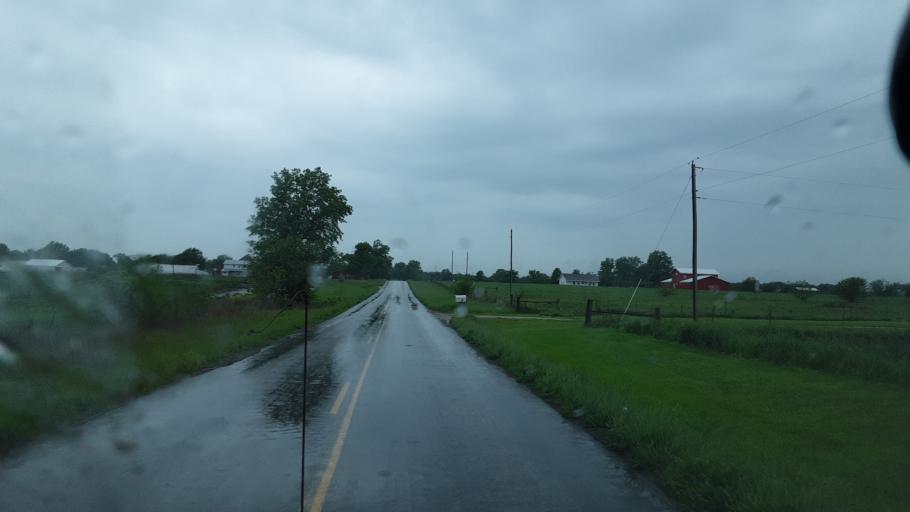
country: US
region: Missouri
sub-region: Randolph County
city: Moberly
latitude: 39.3682
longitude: -92.2593
